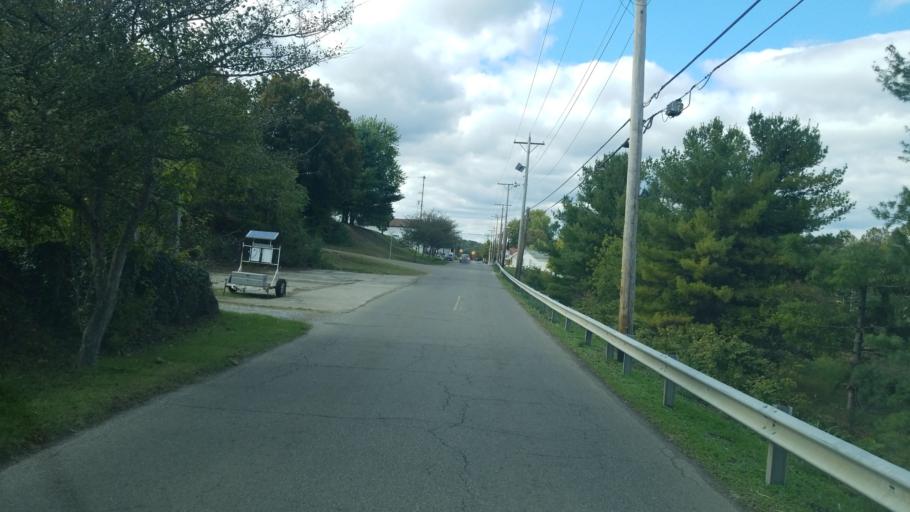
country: US
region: Ohio
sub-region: Jackson County
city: Jackson
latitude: 39.0515
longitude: -82.6341
